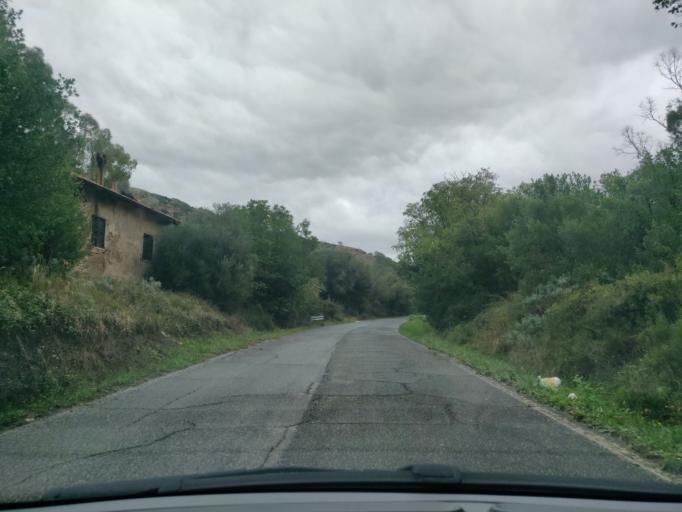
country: IT
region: Latium
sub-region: Citta metropolitana di Roma Capitale
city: Allumiere
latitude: 42.1261
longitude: 11.8565
